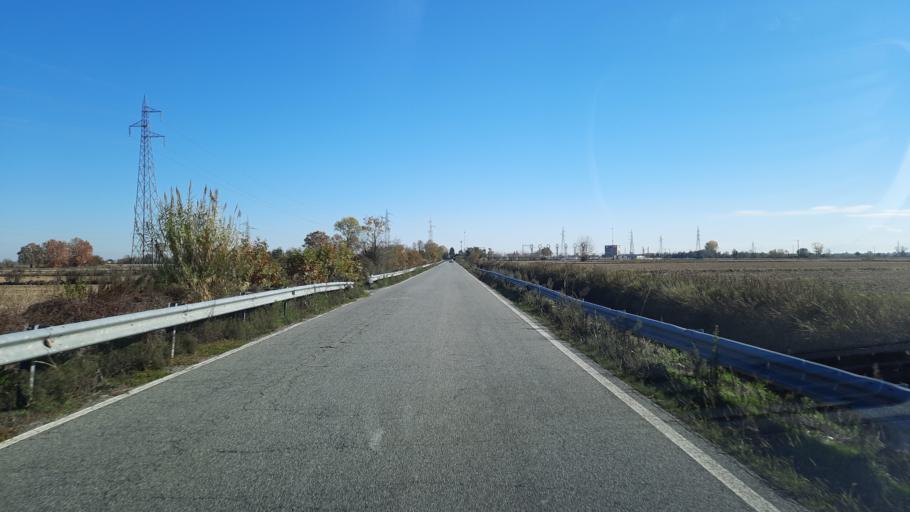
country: IT
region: Piedmont
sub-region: Provincia di Alessandria
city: Balzola
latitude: 45.1870
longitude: 8.4193
